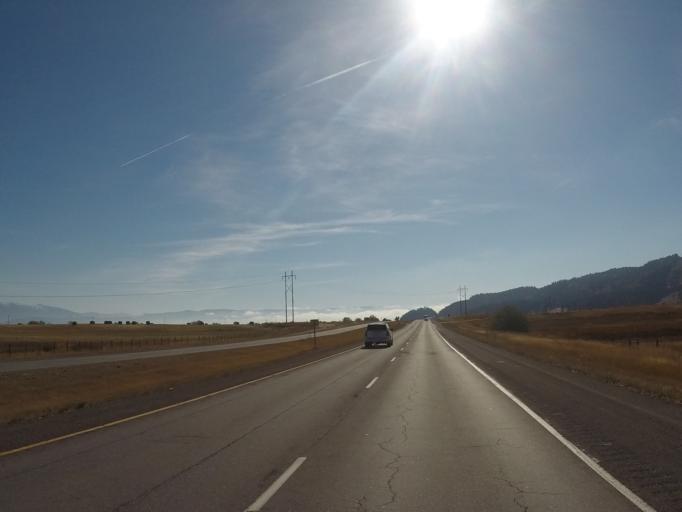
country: US
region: Montana
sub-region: Flathead County
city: Somers
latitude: 48.1141
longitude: -114.2529
